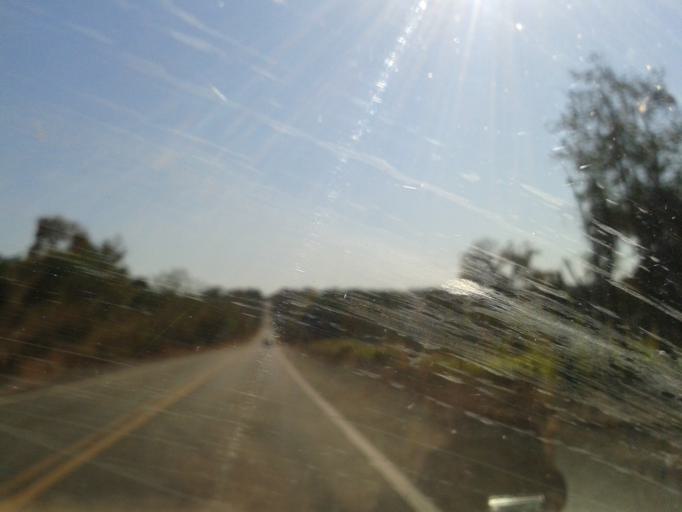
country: BR
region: Goias
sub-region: Mozarlandia
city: Mozarlandia
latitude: -14.8329
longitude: -50.5371
